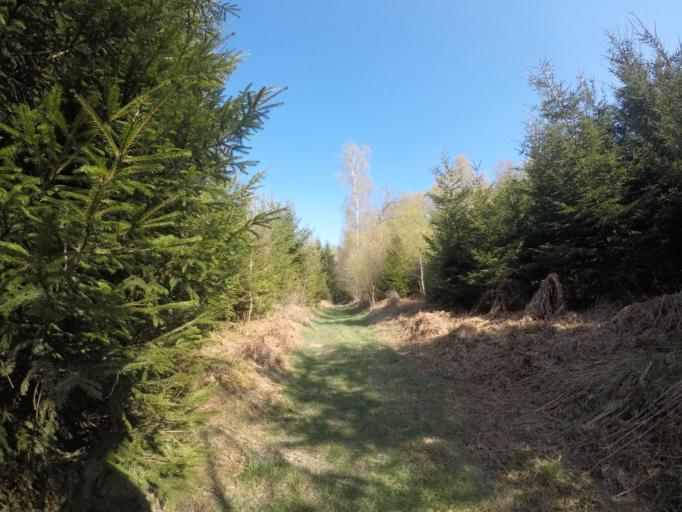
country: BE
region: Wallonia
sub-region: Province du Luxembourg
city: Leglise
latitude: 49.7929
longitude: 5.5853
